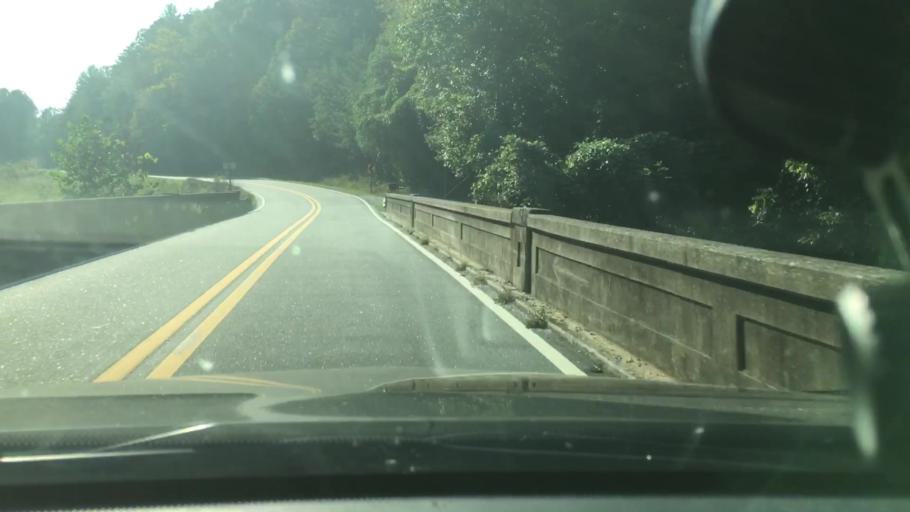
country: US
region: North Carolina
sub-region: Rutherford County
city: Rutherfordton
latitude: 35.3265
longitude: -82.0730
